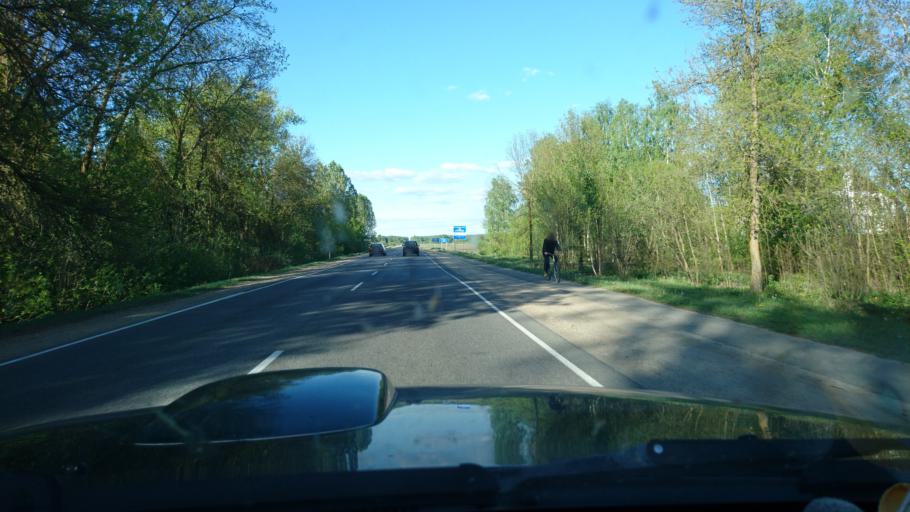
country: BY
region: Brest
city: Byaroza
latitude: 52.5486
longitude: 25.0133
